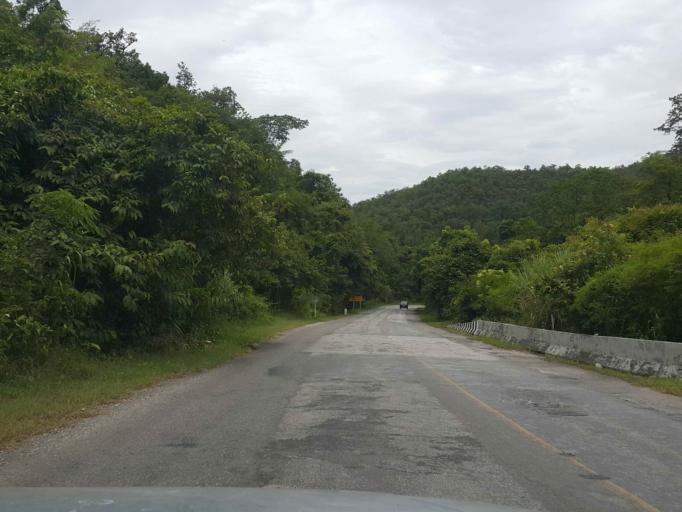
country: TH
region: Lampang
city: Thoen
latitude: 17.6338
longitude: 99.3111
